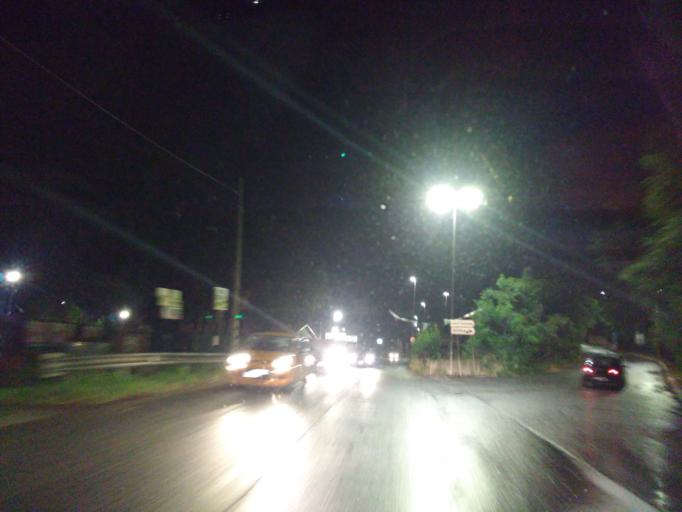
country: IT
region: Latium
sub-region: Citta metropolitana di Roma Capitale
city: Vitinia
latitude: 41.7871
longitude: 12.4271
